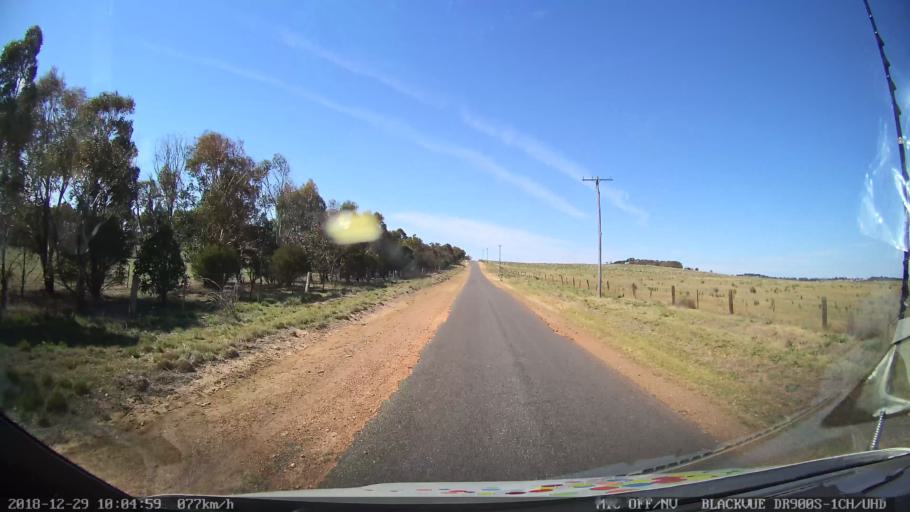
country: AU
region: New South Wales
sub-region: Goulburn Mulwaree
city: Goulburn
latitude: -34.8283
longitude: 149.4541
